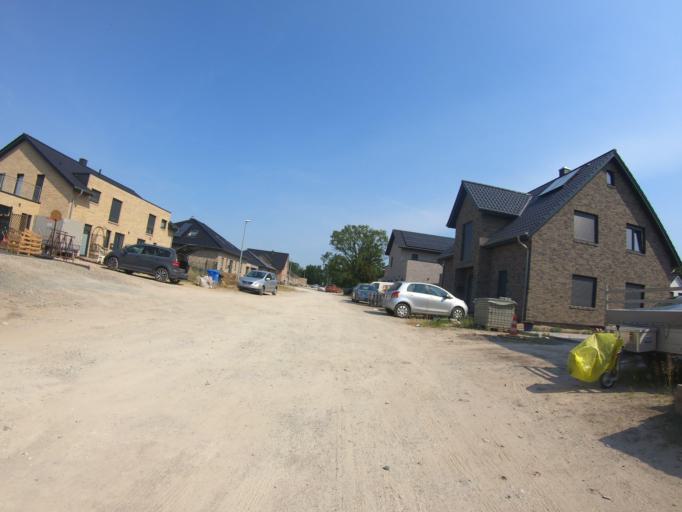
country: DE
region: Lower Saxony
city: Gifhorn
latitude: 52.4763
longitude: 10.5739
